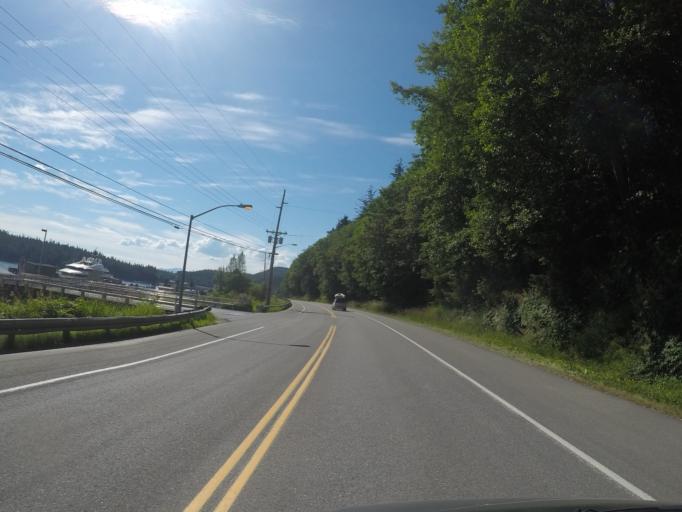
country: US
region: Alaska
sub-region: Juneau City and Borough
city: Juneau
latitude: 58.3823
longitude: -134.6767
